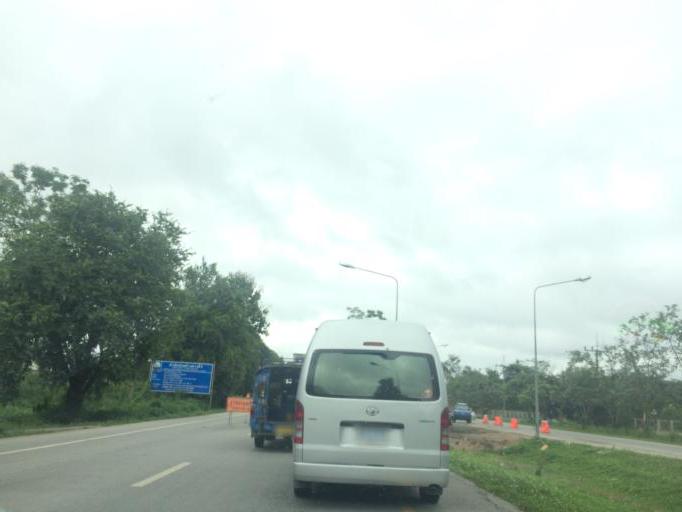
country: TH
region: Chiang Rai
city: Chiang Rai
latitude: 19.8417
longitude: 99.7972
